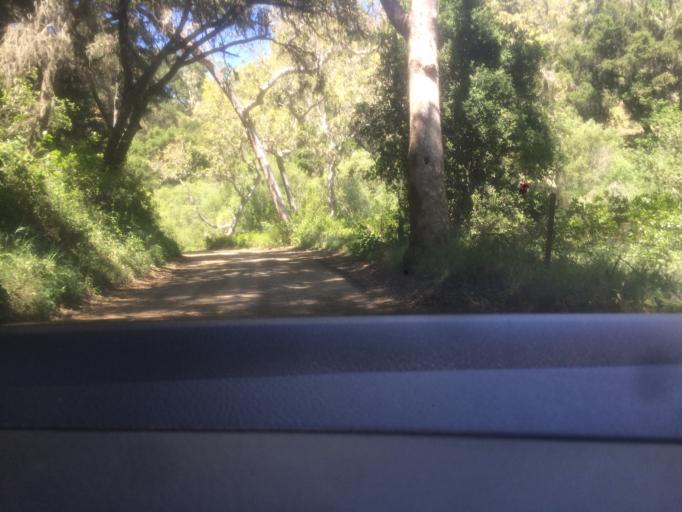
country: US
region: California
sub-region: San Luis Obispo County
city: Templeton
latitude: 35.5246
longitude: -120.7898
